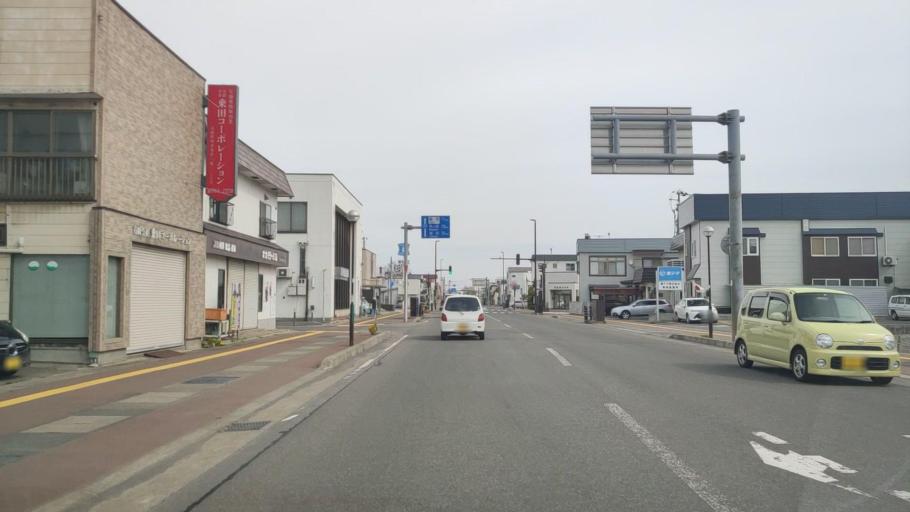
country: JP
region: Aomori
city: Aomori Shi
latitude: 40.8267
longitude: 140.7284
